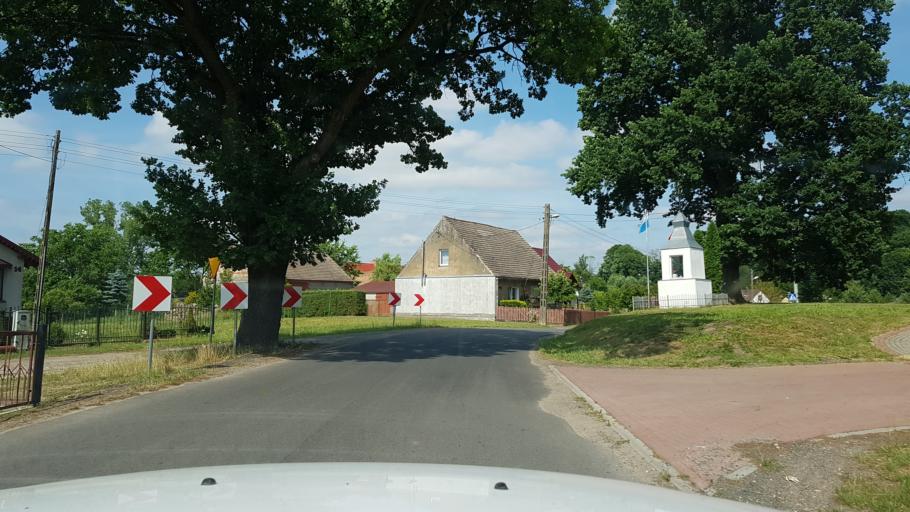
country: PL
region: West Pomeranian Voivodeship
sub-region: Powiat goleniowski
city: Osina
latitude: 53.6023
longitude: 15.0046
